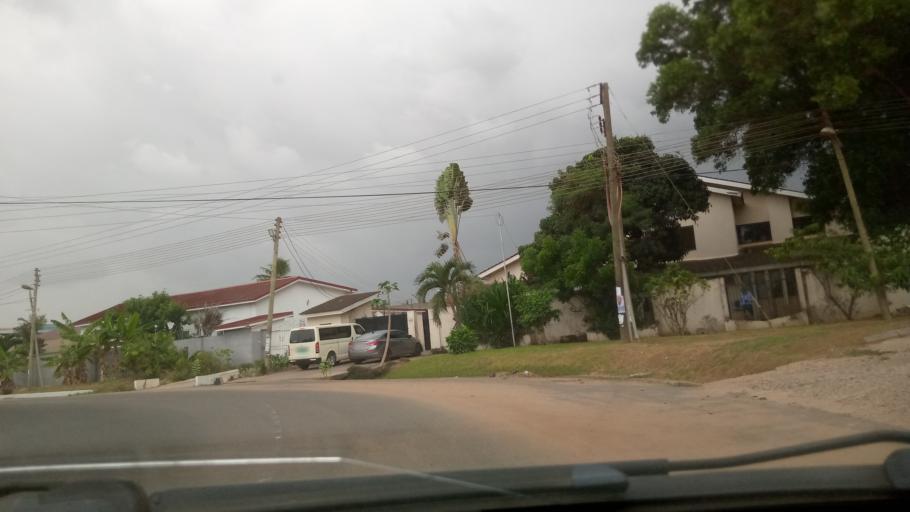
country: GH
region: Greater Accra
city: Dome
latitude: 5.6160
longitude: -0.1968
